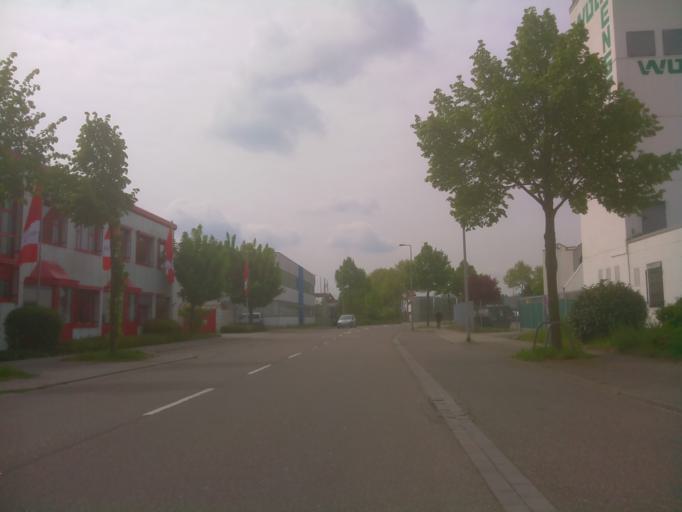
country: DE
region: Baden-Wuerttemberg
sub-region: Karlsruhe Region
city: Ilvesheim
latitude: 49.4437
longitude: 8.5738
